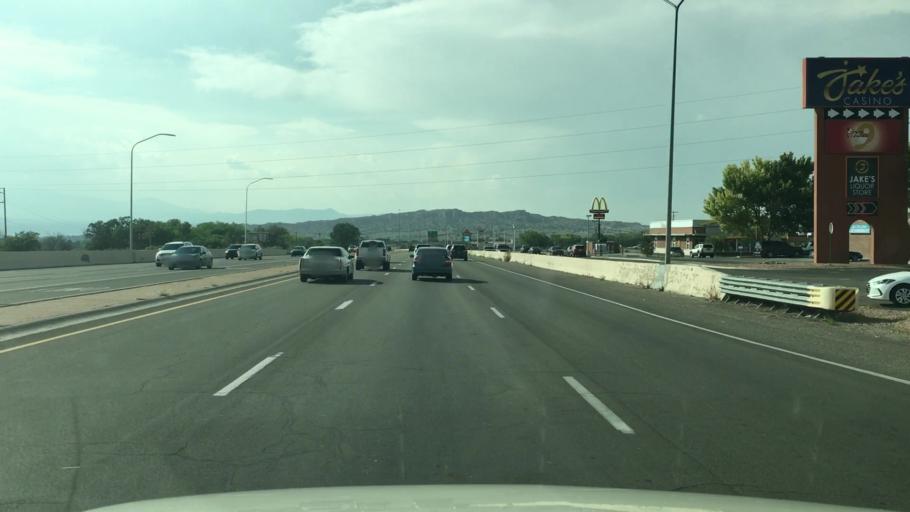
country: US
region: New Mexico
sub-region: Santa Fe County
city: Pojoaque
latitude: 35.8830
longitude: -106.0143
